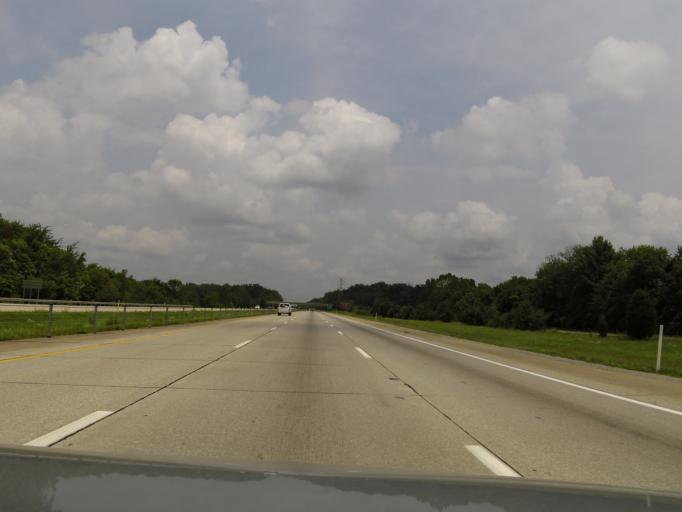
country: US
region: Kentucky
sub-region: Bullitt County
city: Lebanon Junction
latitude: 37.9028
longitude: -85.6944
